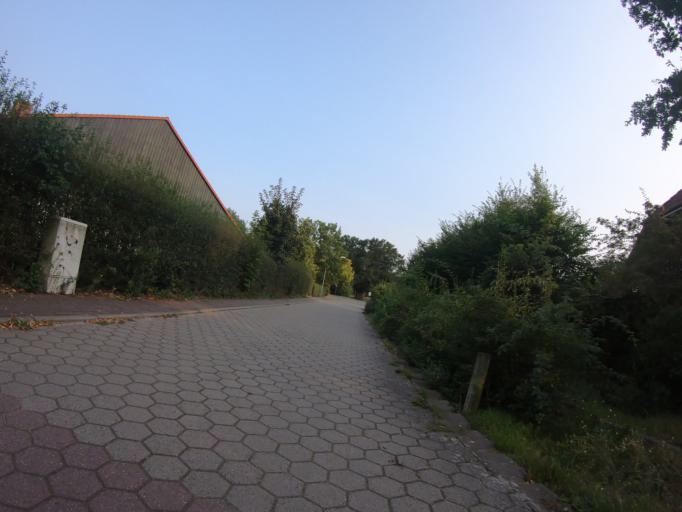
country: DE
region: Lower Saxony
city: Leiferde
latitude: 52.4477
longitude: 10.4351
